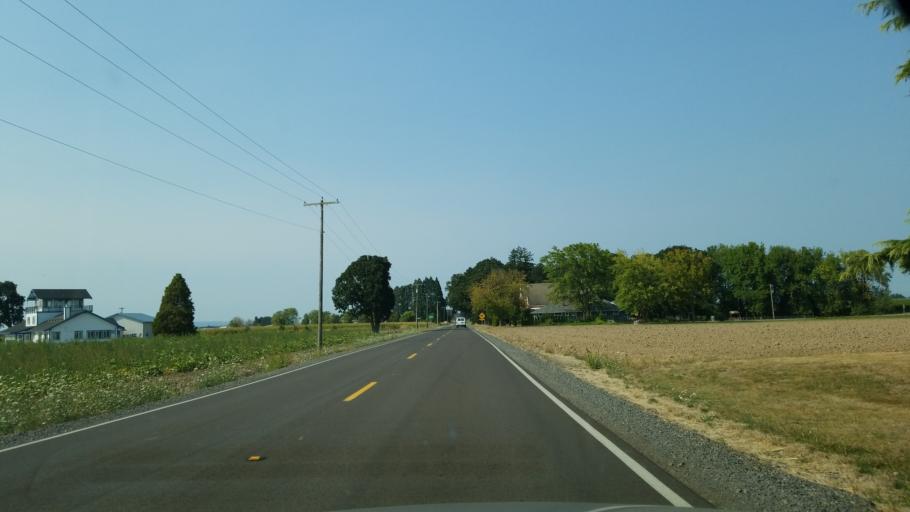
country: US
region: Oregon
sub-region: Marion County
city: Mount Angel
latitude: 45.0691
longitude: -122.7435
